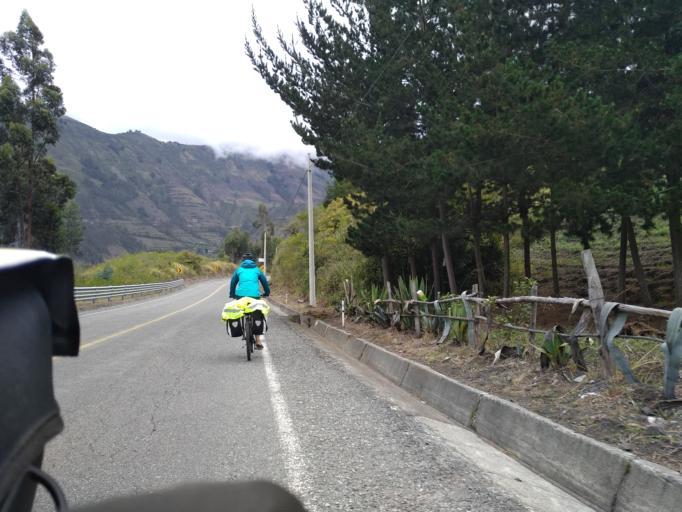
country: EC
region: Chimborazo
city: Guano
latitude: -1.5529
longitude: -78.5337
